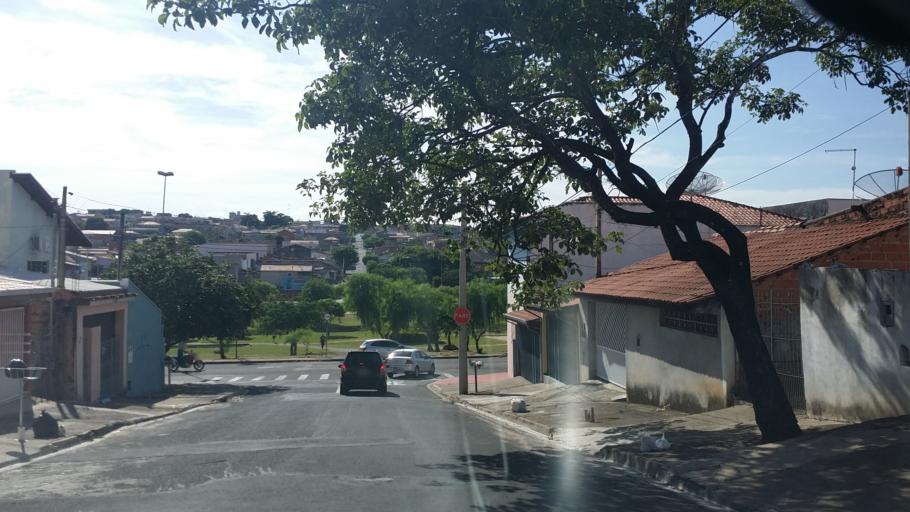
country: BR
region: Sao Paulo
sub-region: Indaiatuba
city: Indaiatuba
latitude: -23.1233
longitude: -47.2348
